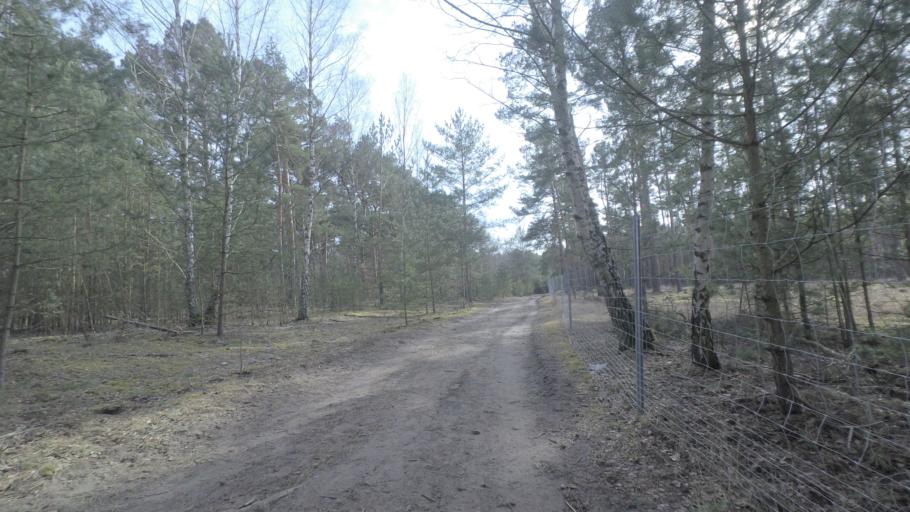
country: DE
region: Brandenburg
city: Ludwigsfelde
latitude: 52.3066
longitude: 13.2262
